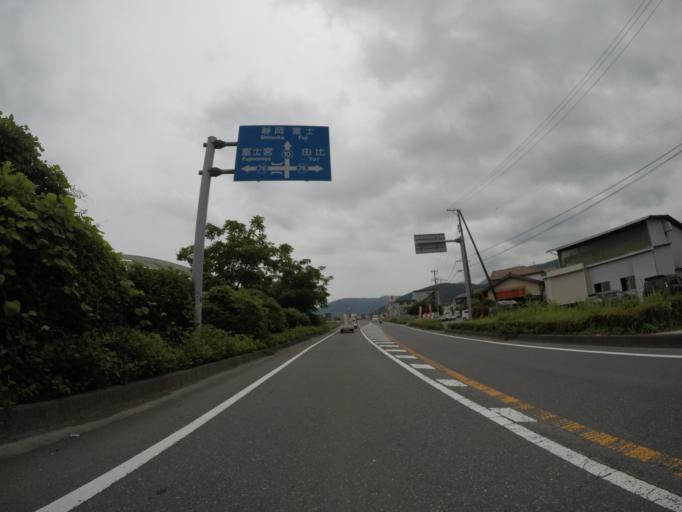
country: JP
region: Shizuoka
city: Fujinomiya
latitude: 35.1942
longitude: 138.5884
